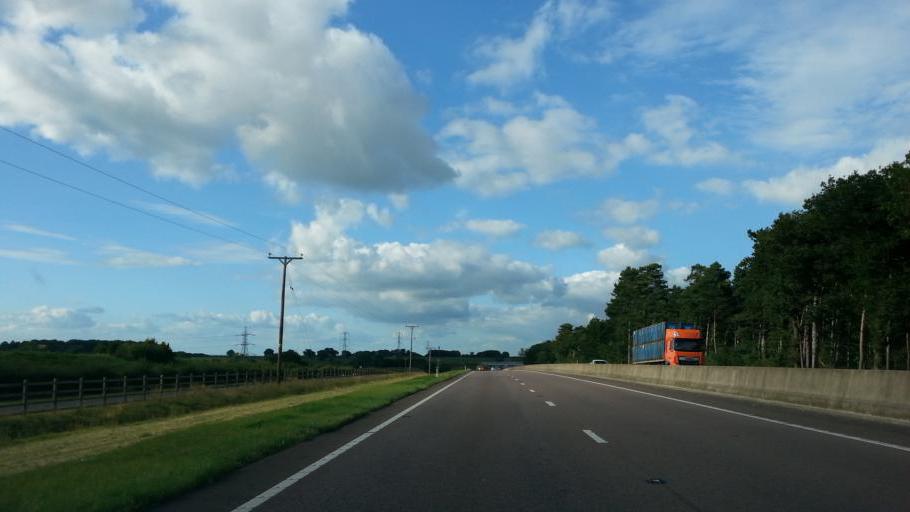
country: GB
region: England
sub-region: Nottinghamshire
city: Cotgrave
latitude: 52.8903
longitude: -1.0248
